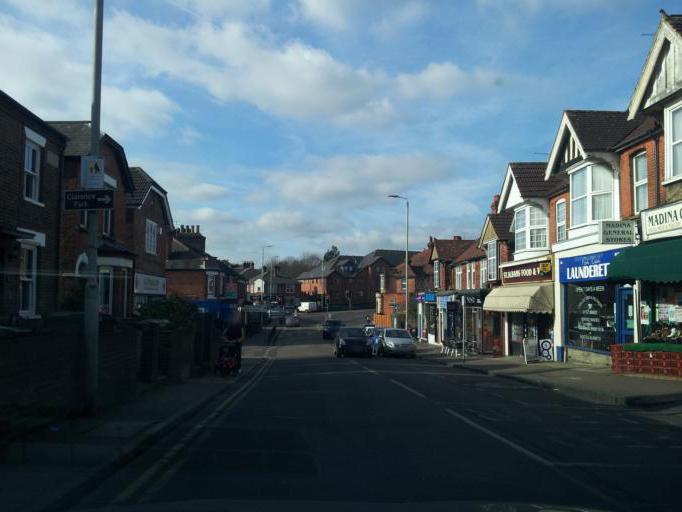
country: GB
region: England
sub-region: Hertfordshire
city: St Albans
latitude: 51.7518
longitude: -0.3220
